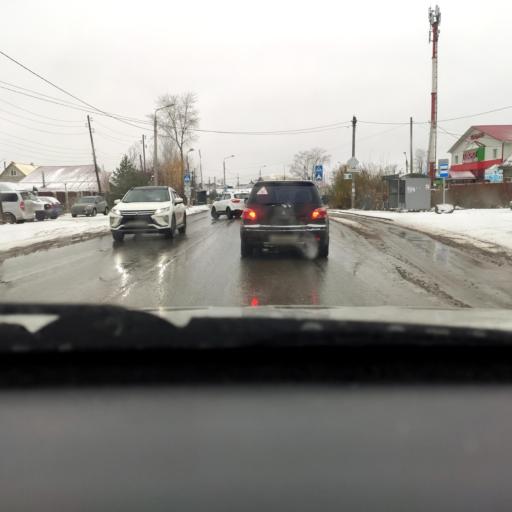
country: RU
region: Perm
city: Froly
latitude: 57.9771
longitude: 56.3082
